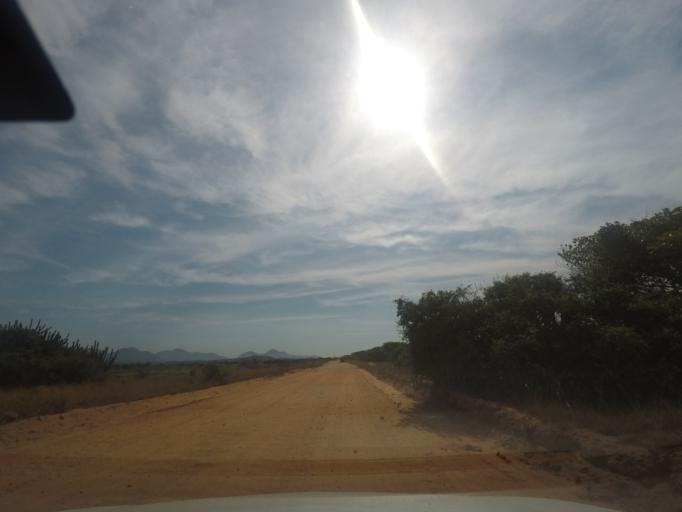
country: BR
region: Rio de Janeiro
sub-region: Marica
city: Marica
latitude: -22.9606
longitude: -42.8532
